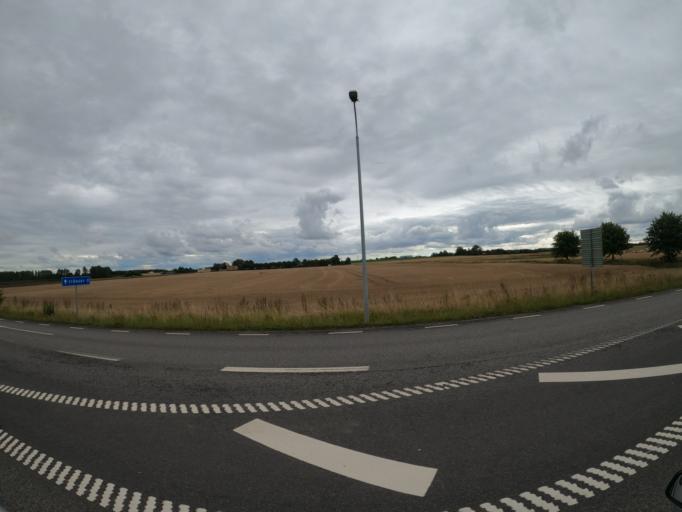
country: SE
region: Skane
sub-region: Lunds Kommun
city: Lund
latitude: 55.7433
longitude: 13.1993
